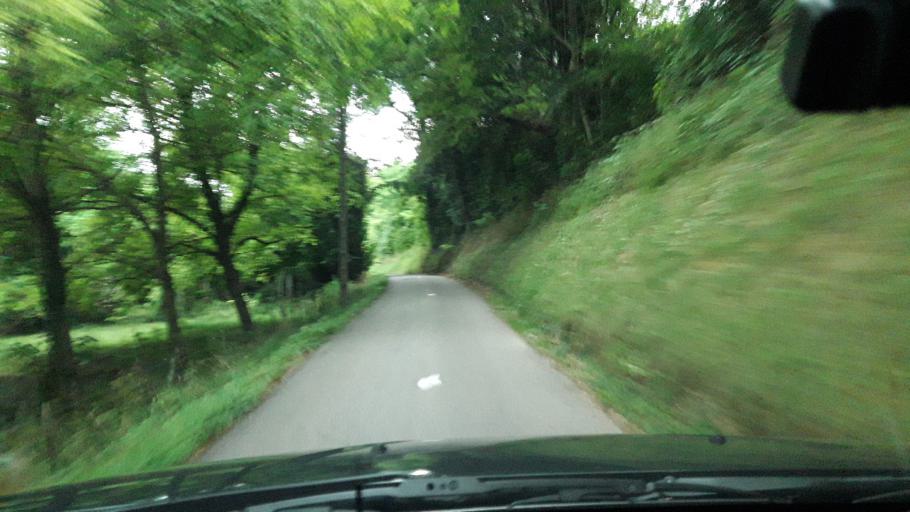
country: FR
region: Rhone-Alpes
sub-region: Departement de la Savoie
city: Barberaz
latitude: 45.5326
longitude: 5.9286
